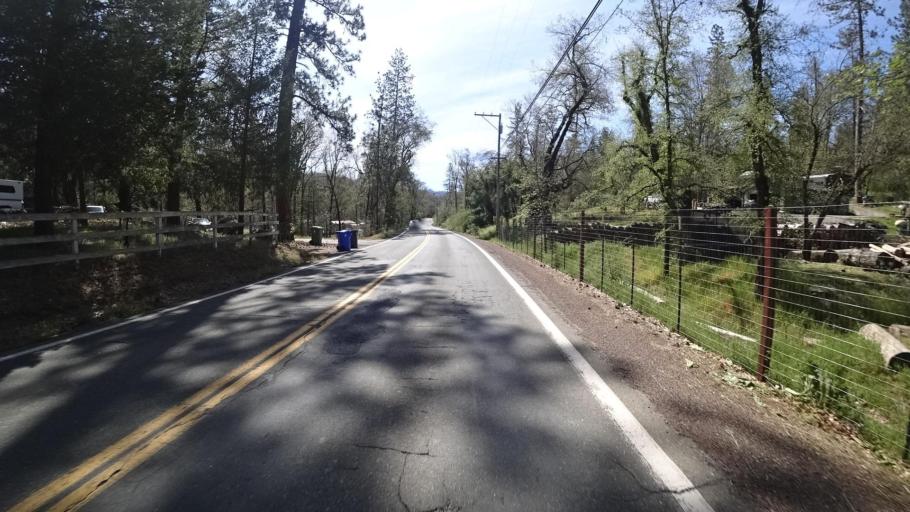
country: US
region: California
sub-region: Lake County
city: Cobb
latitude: 38.8464
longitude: -122.7538
